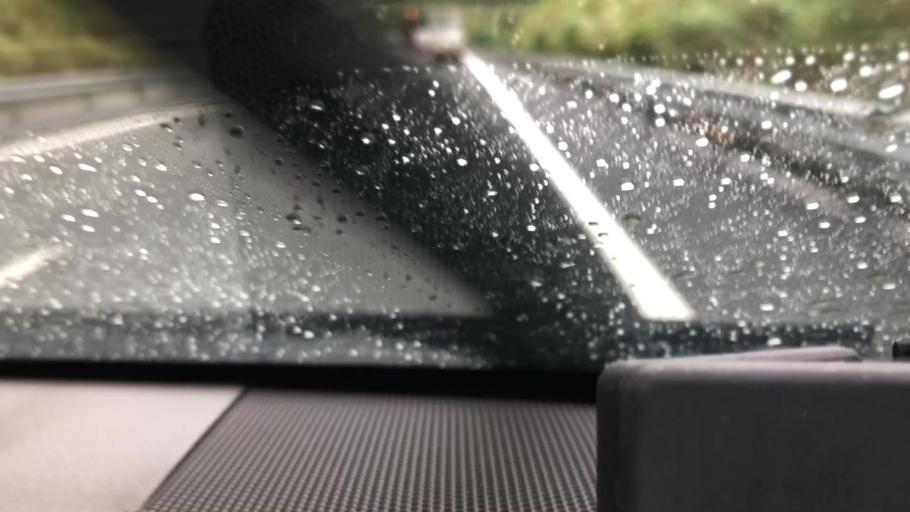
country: JP
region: Shizuoka
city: Mishima
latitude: 35.1739
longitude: 138.8843
